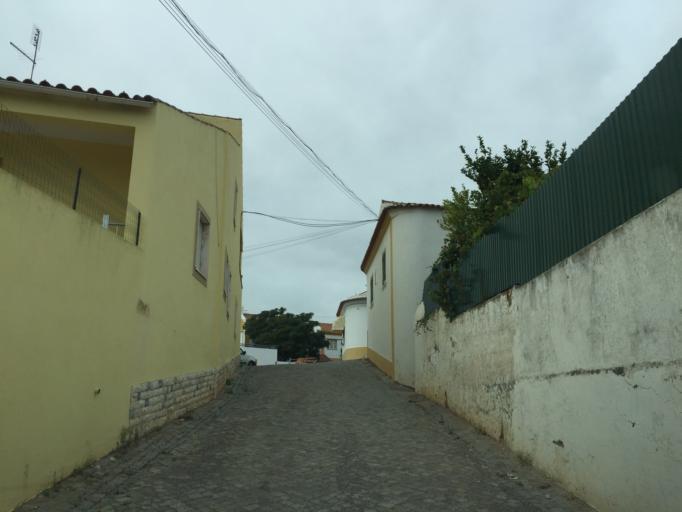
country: PT
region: Portalegre
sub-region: Avis
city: Avis
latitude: 39.0550
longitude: -7.8894
